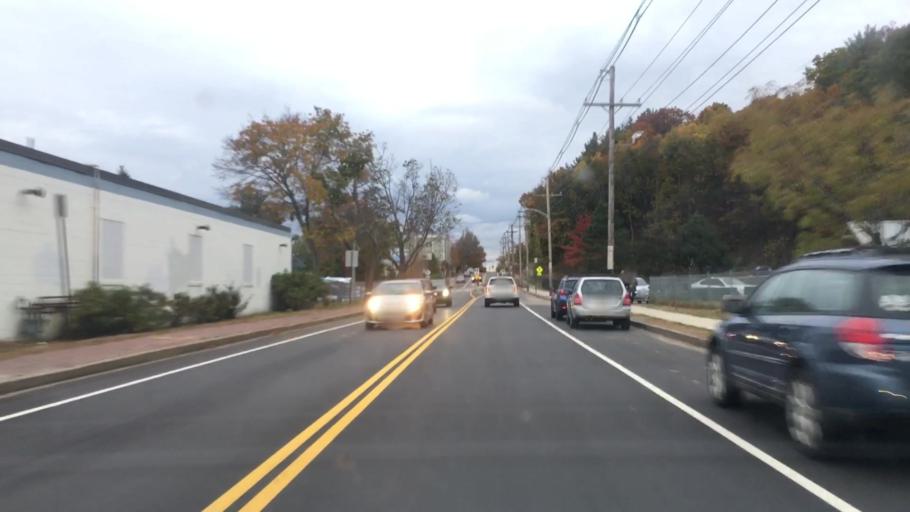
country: US
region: Maine
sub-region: Cumberland County
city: Portland
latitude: 43.6483
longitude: -70.2775
